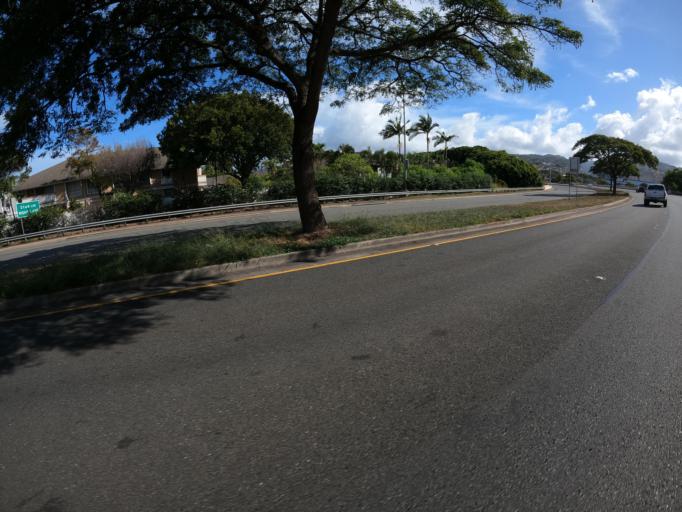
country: US
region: Hawaii
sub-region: Honolulu County
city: Halawa
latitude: 21.3691
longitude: -157.9209
